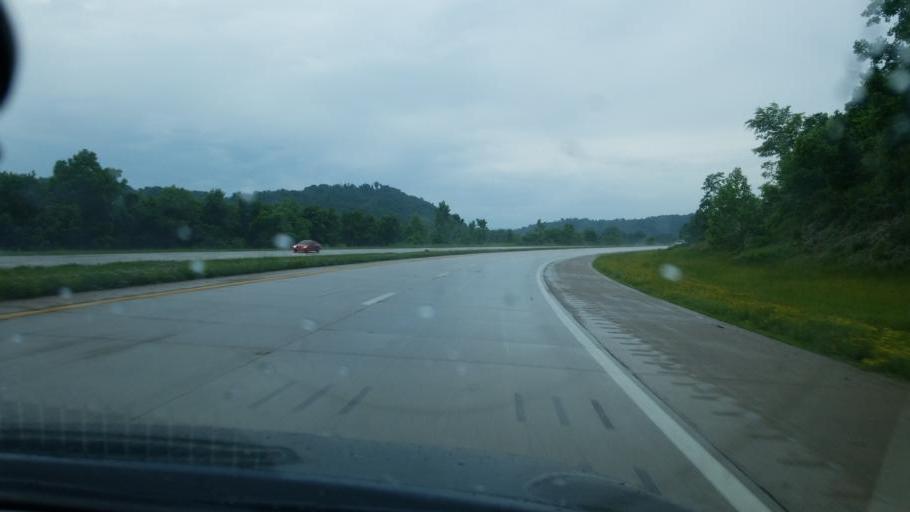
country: US
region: Ohio
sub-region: Athens County
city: Athens
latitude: 39.3049
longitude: -81.9605
